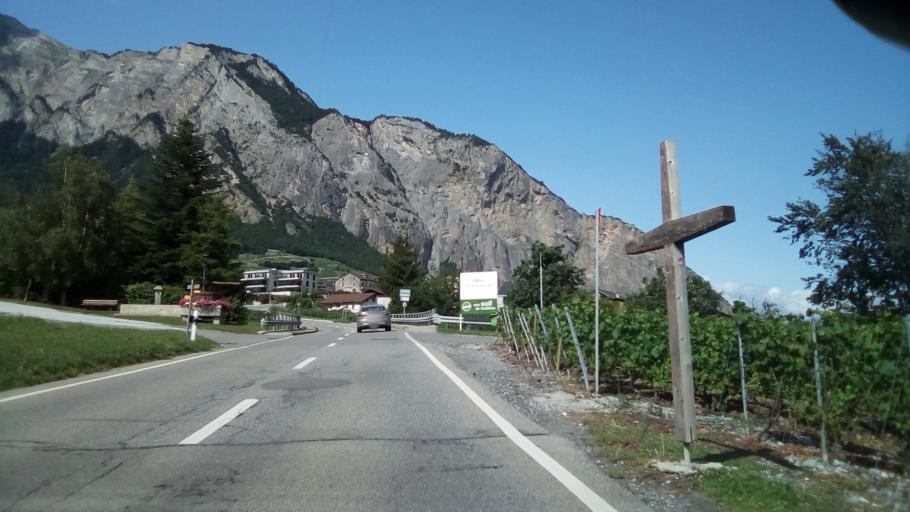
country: CH
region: Valais
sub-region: Conthey District
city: Chamoson
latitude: 46.1962
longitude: 7.2201
